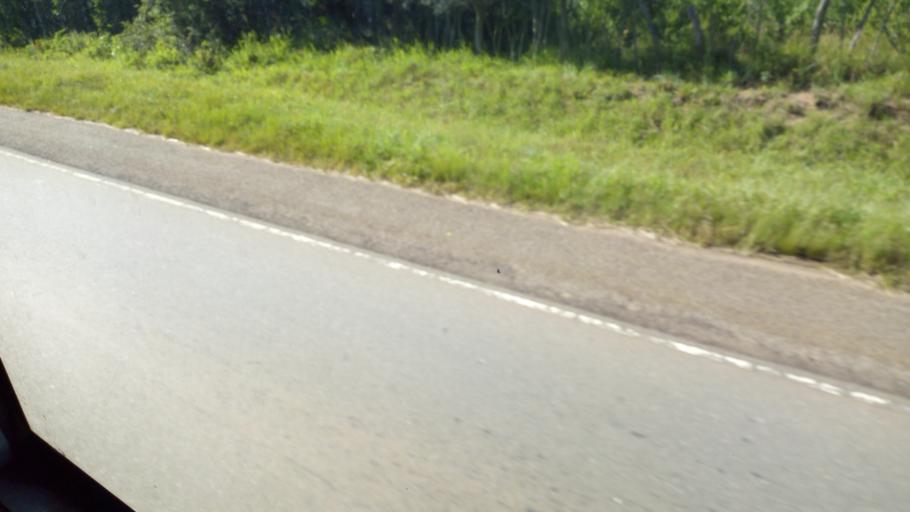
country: UG
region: Central Region
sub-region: Lyantonde District
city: Lyantonde
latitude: -0.4441
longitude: 31.0709
